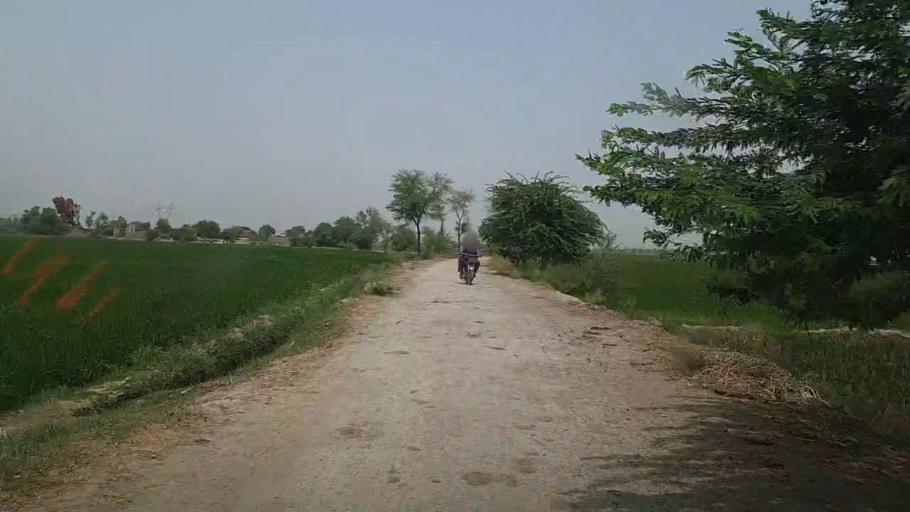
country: PK
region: Sindh
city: Sita Road
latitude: 27.0641
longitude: 67.8490
